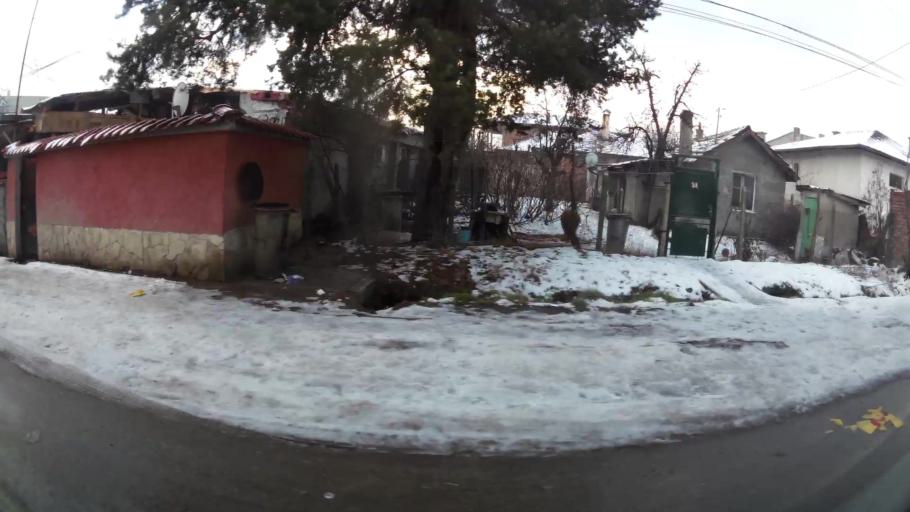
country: BG
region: Sofia-Capital
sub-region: Stolichna Obshtina
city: Sofia
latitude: 42.6965
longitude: 23.2726
